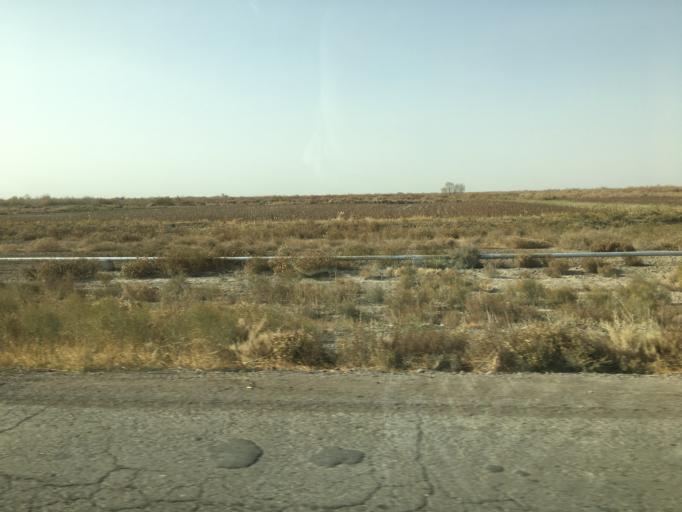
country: TM
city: Akdepe
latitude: 41.6516
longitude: 58.6670
